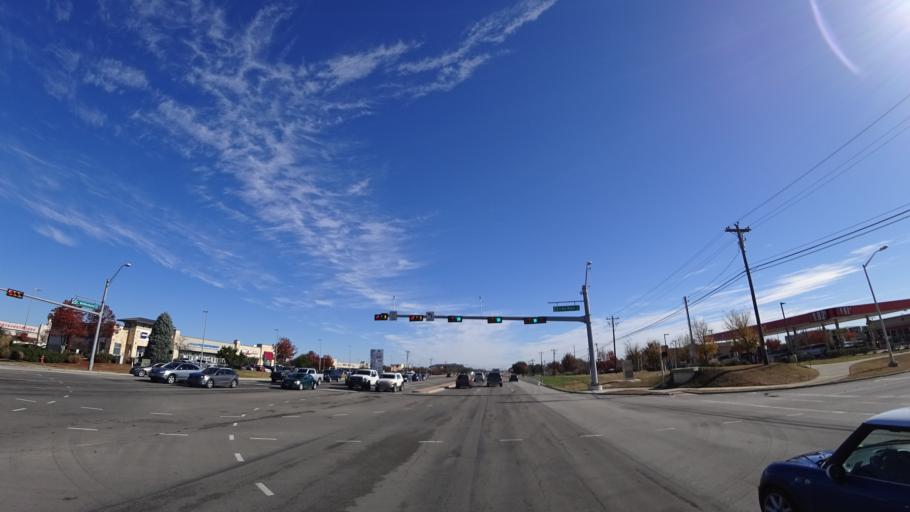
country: US
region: Texas
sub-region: Williamson County
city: Cedar Park
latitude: 30.5266
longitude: -97.8111
